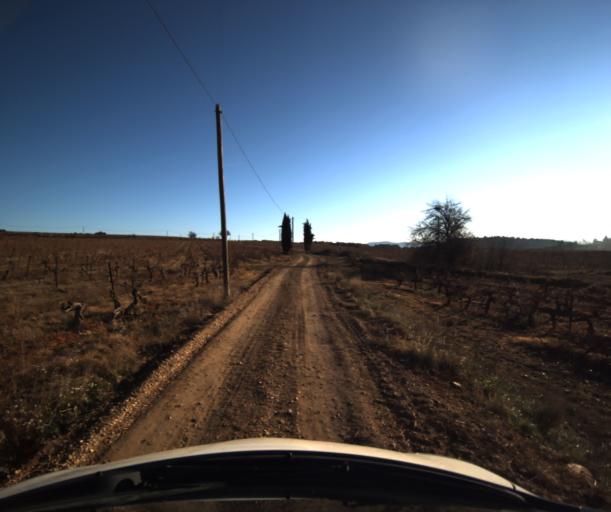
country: FR
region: Provence-Alpes-Cote d'Azur
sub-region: Departement du Vaucluse
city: Ansouis
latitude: 43.7228
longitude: 5.4864
